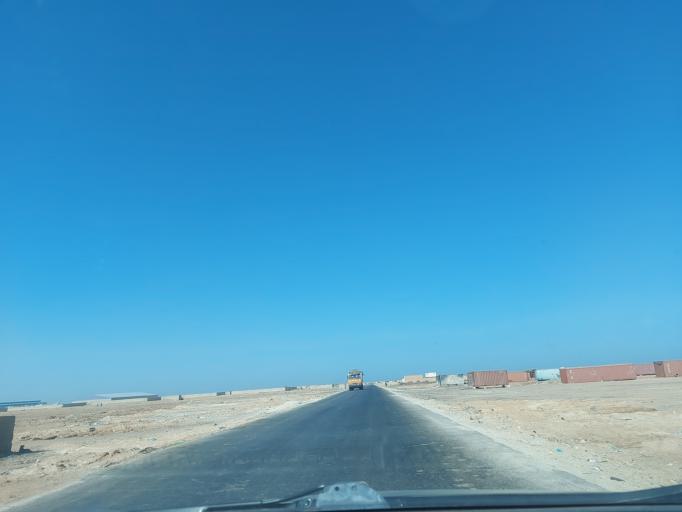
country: MR
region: Nouakchott
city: Nouakchott
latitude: 18.0581
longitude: -16.0141
